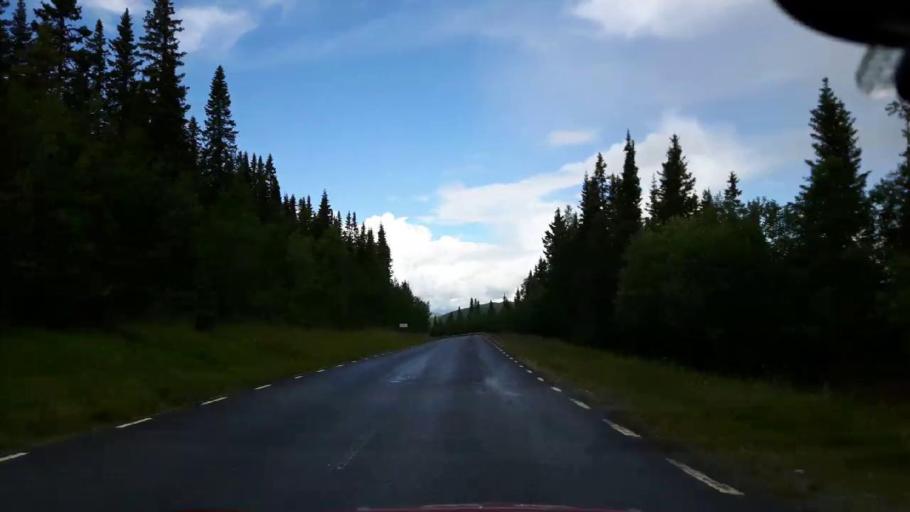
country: SE
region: Vaesterbotten
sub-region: Vilhelmina Kommun
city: Sjoberg
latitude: 64.9994
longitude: 15.1999
